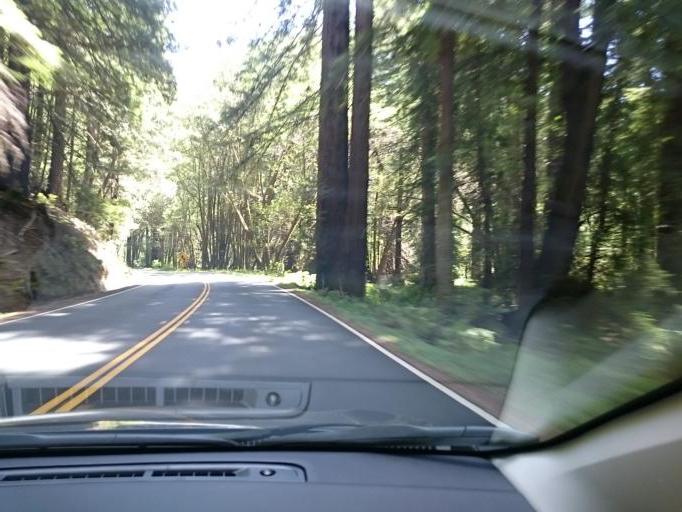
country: US
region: California
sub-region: Mendocino County
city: Boonville
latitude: 39.1551
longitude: -123.6220
